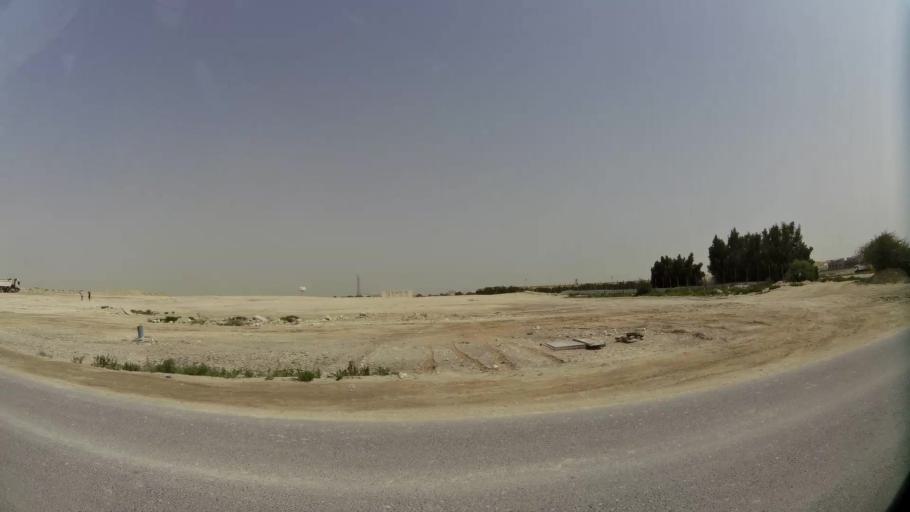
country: QA
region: Baladiyat ar Rayyan
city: Ar Rayyan
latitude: 25.2333
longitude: 51.4069
